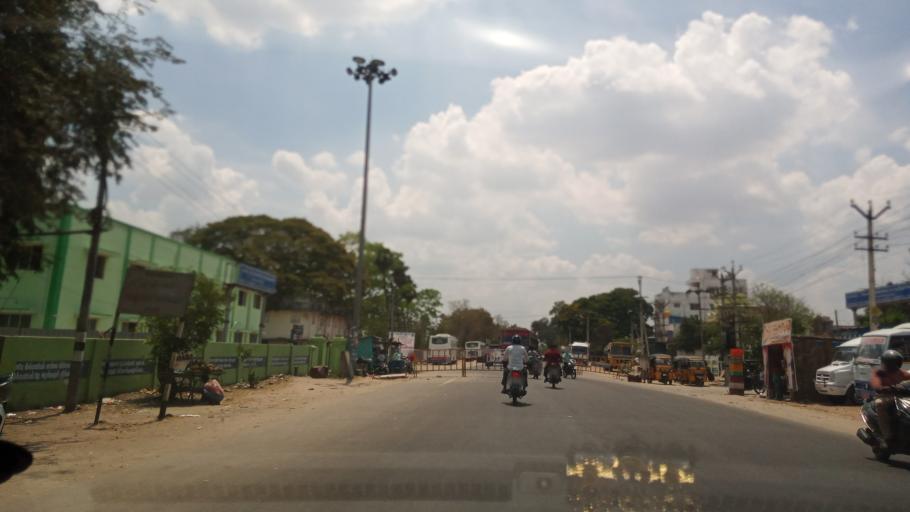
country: IN
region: Tamil Nadu
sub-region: Vellore
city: Walajapet
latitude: 12.9256
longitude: 79.3575
